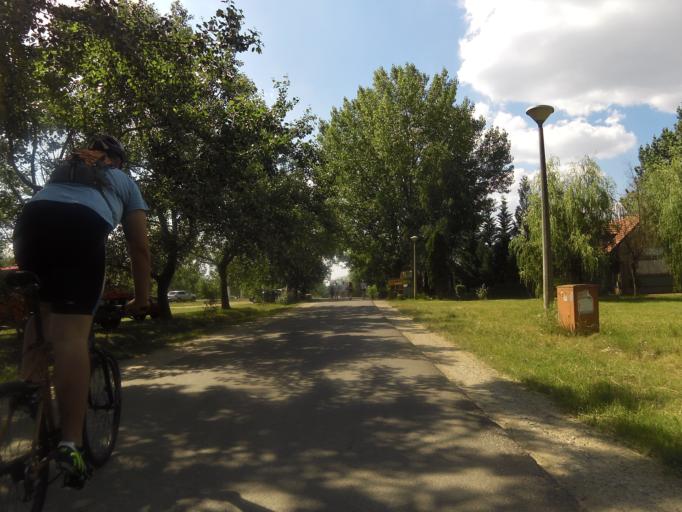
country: HU
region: Jasz-Nagykun-Szolnok
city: Tiszafured
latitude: 47.6239
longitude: 20.7332
